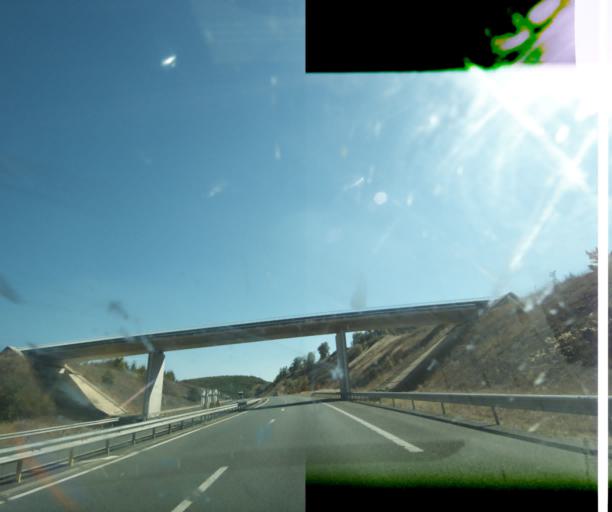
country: FR
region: Midi-Pyrenees
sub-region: Departement du Lot
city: Souillac
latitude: 44.8428
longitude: 1.4915
